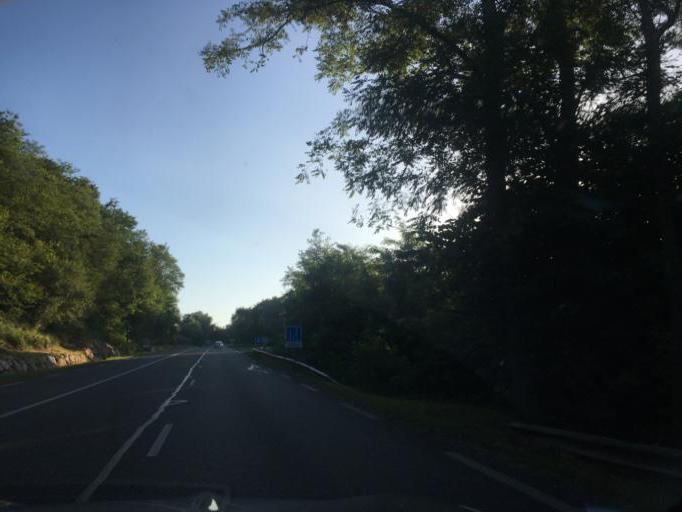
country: FR
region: Midi-Pyrenees
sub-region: Departement des Hautes-Pyrenees
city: Ibos
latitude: 43.2409
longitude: -0.0234
